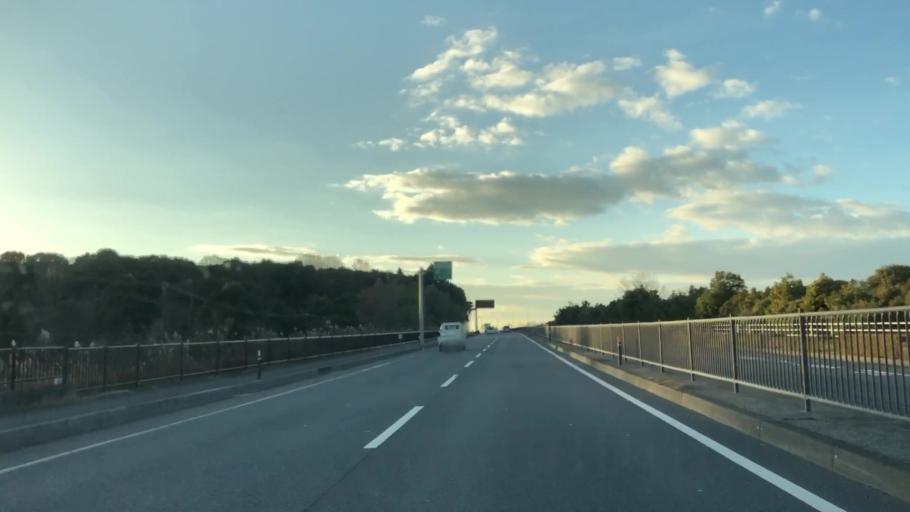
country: JP
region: Fukuoka
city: Nakatsu
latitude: 33.5538
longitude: 131.2567
